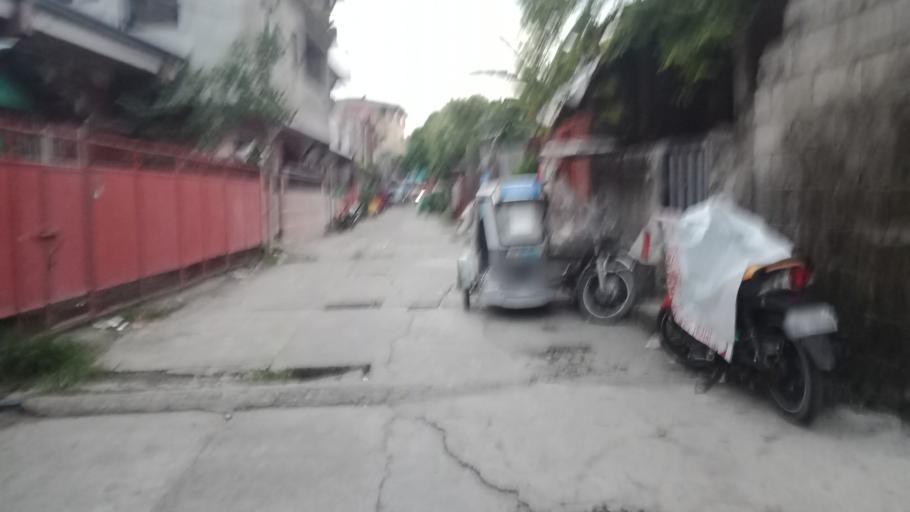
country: PH
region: Calabarzon
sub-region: Province of Rizal
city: Pateros
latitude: 14.5450
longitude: 121.1013
